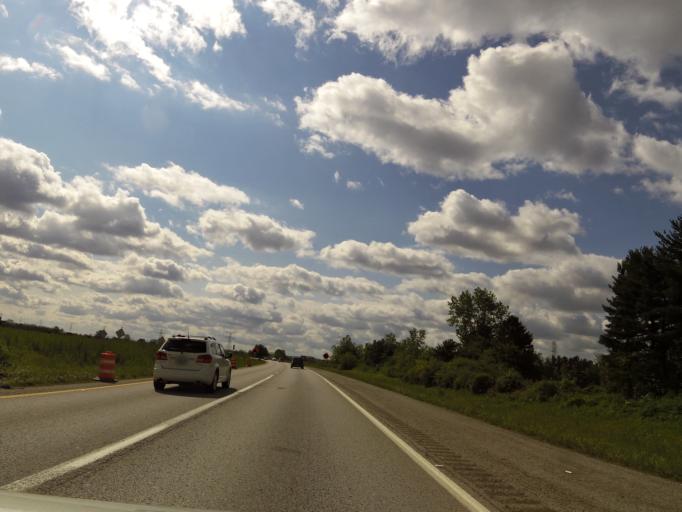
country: US
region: Ohio
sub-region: Franklin County
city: Groveport
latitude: 39.8695
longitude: -82.8541
